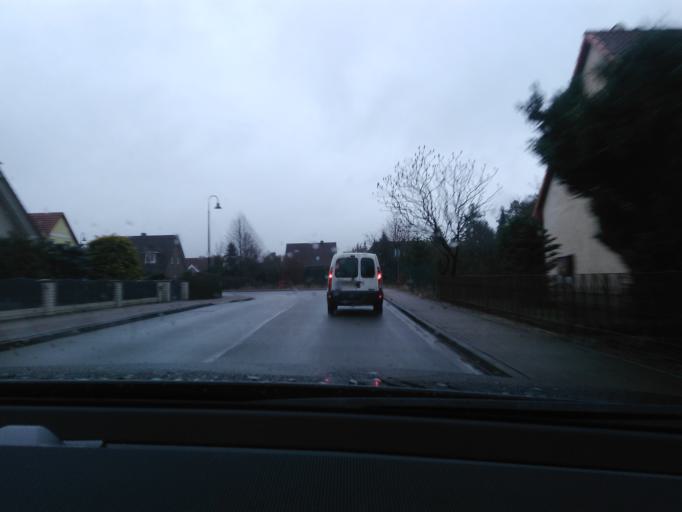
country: DE
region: Brandenburg
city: Wittstock
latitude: 53.1745
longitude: 12.4827
